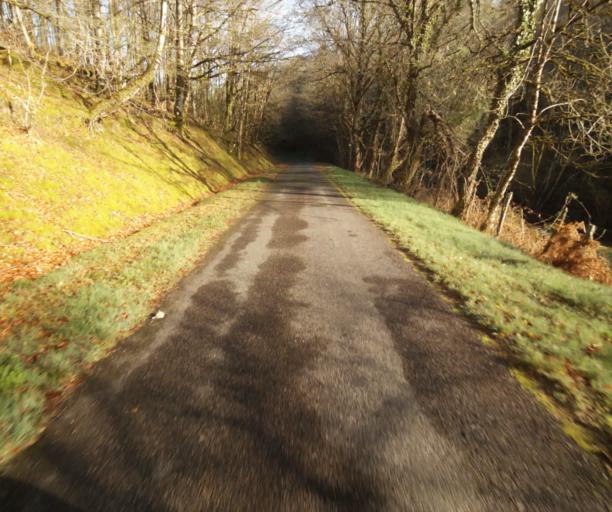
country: FR
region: Limousin
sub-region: Departement de la Correze
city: Correze
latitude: 45.2972
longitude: 1.8547
